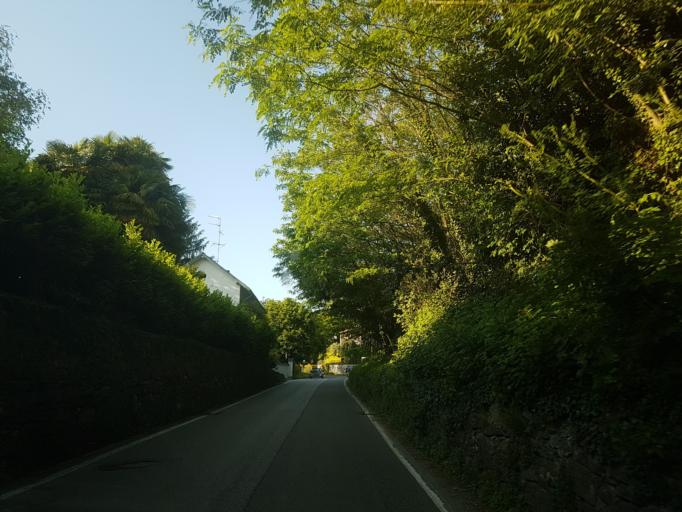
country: IT
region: Lombardy
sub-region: Provincia di Lecco
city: Vergano-Villa
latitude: 45.8032
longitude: 9.3636
